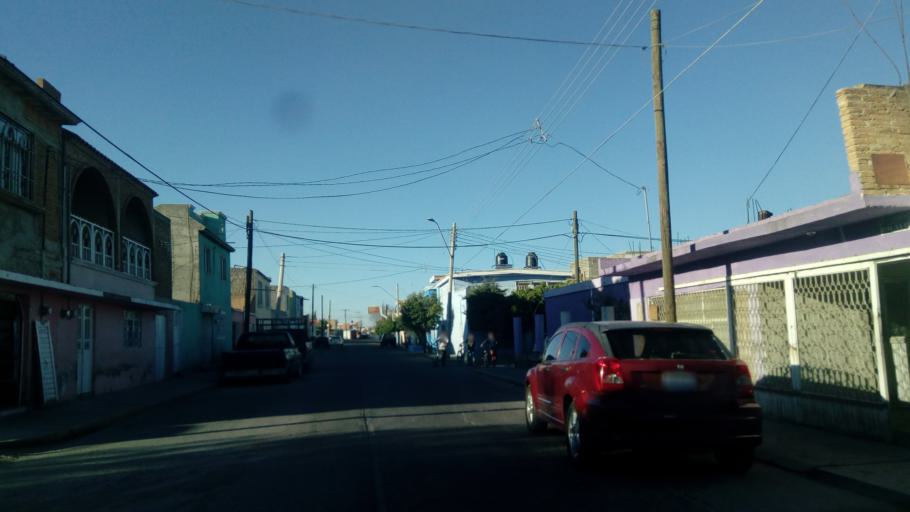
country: MX
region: Durango
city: Victoria de Durango
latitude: 24.0069
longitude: -104.6723
